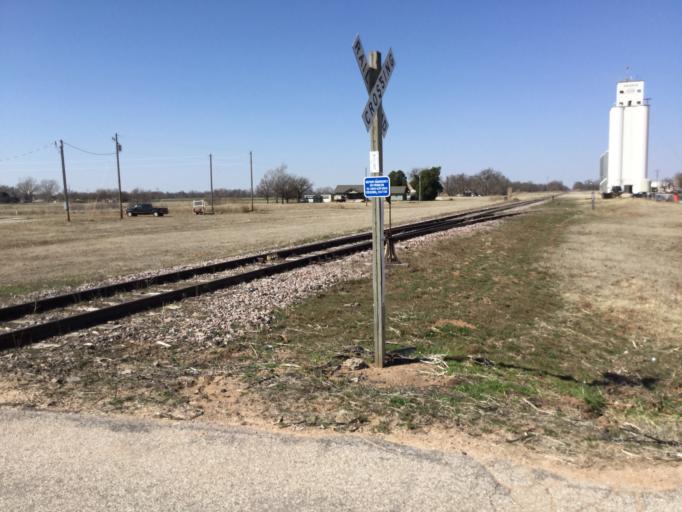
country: US
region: Kansas
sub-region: Barber County
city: Medicine Lodge
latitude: 37.2467
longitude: -98.4177
